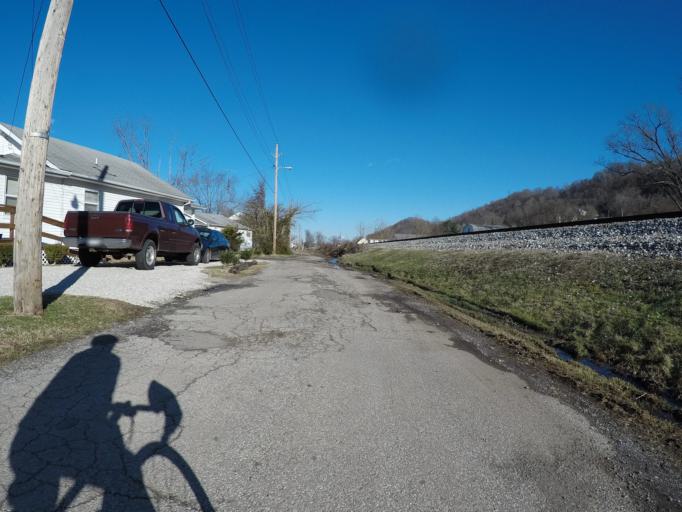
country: US
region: West Virginia
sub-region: Cabell County
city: Pea Ridge
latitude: 38.4281
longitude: -82.3795
